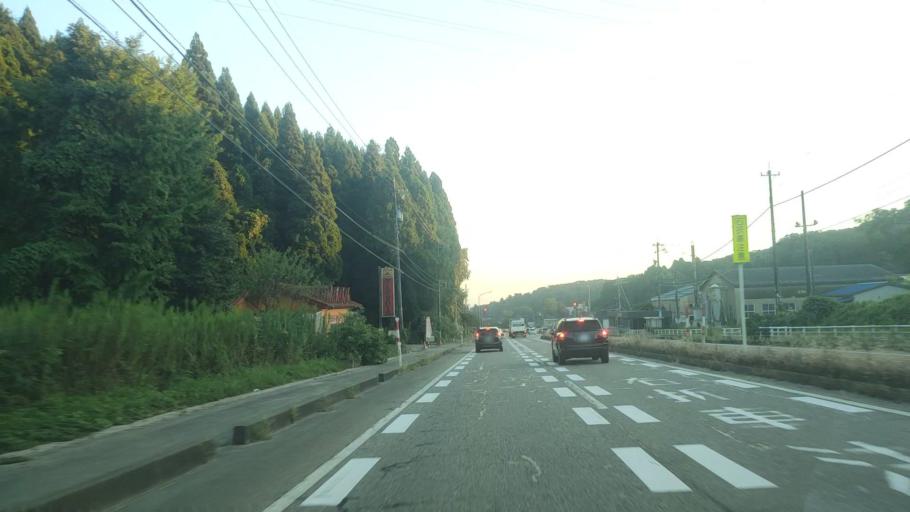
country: JP
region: Toyama
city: Takaoka
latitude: 36.7906
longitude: 137.0011
